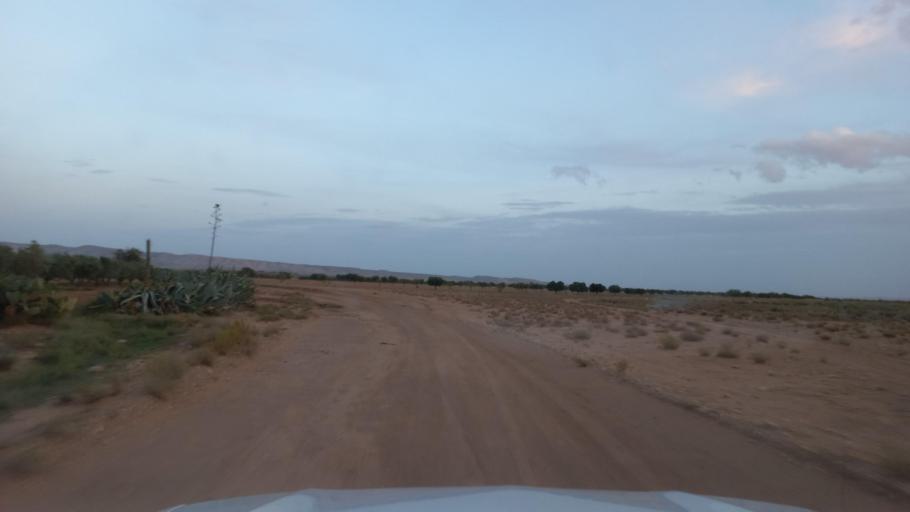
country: TN
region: Al Qasrayn
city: Sbiba
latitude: 35.3493
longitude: 9.0453
